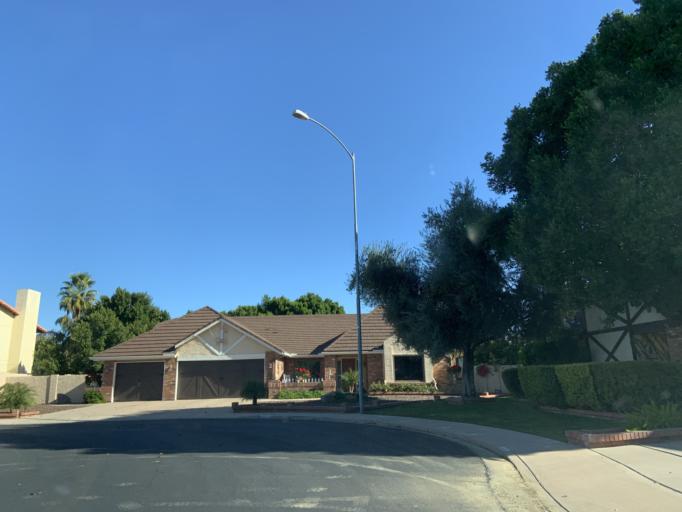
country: US
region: Arizona
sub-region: Maricopa County
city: San Carlos
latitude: 33.3681
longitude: -111.8791
